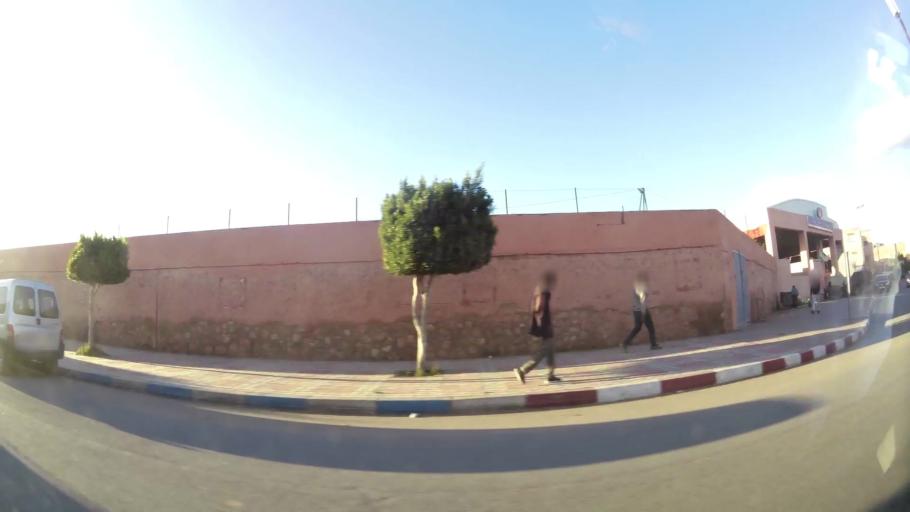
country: MA
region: Marrakech-Tensift-Al Haouz
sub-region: Kelaa-Des-Sraghna
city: Sidi Abdallah
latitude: 32.2396
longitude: -7.9540
